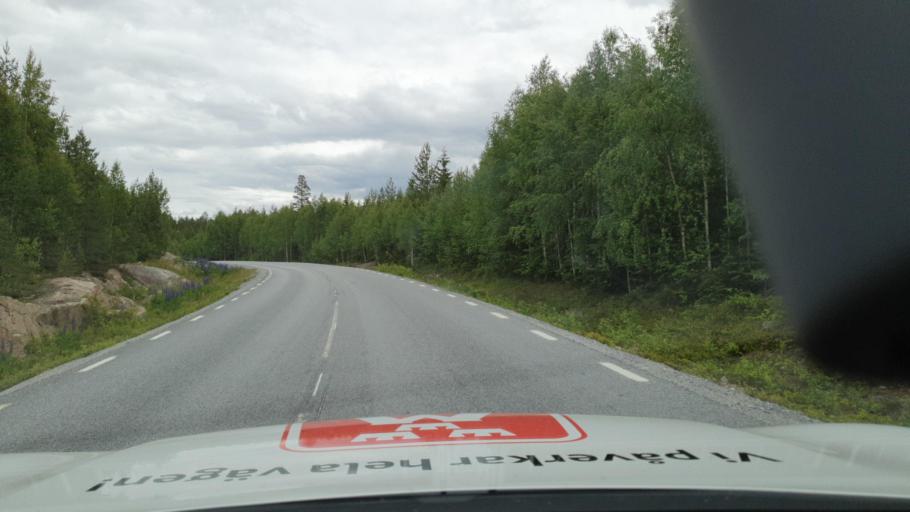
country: SE
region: Vaesterbotten
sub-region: Bjurholms Kommun
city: Bjurholm
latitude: 63.8826
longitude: 19.0319
